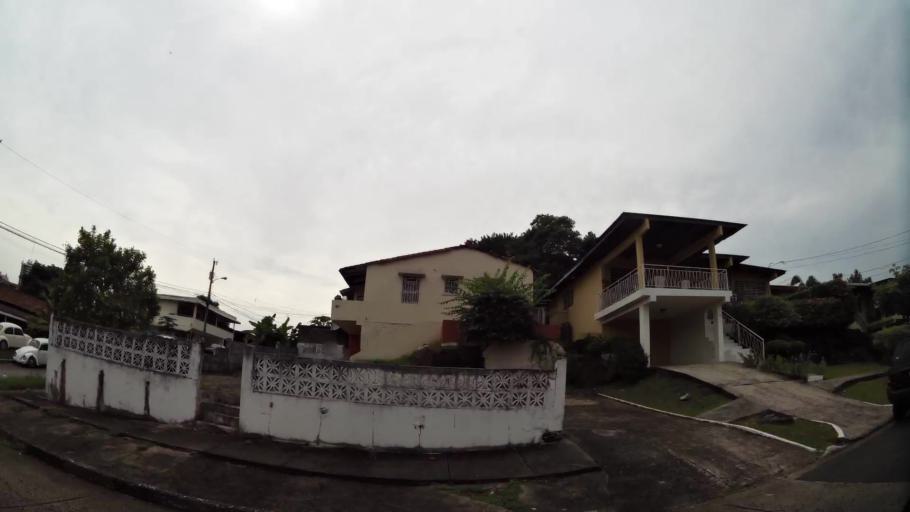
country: PA
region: Panama
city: Panama
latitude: 9.0209
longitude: -79.5187
